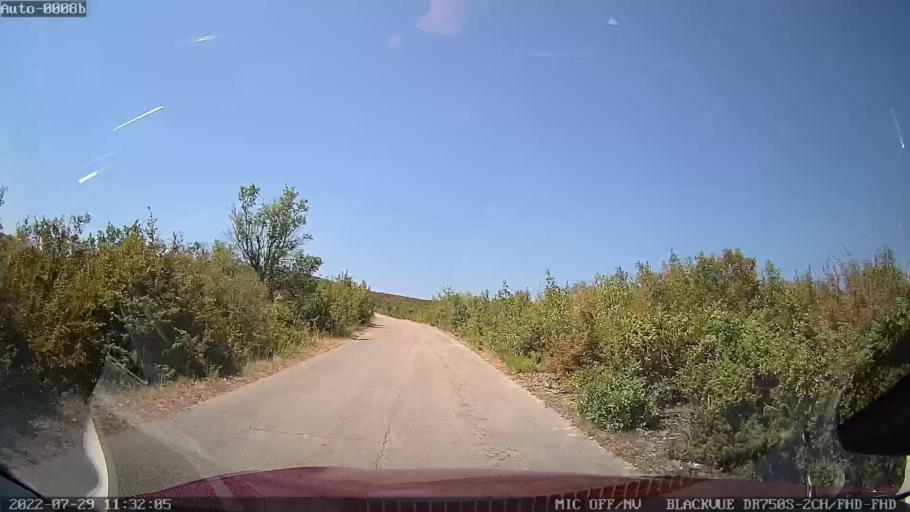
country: HR
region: Zadarska
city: Obrovac
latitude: 44.1927
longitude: 15.7426
